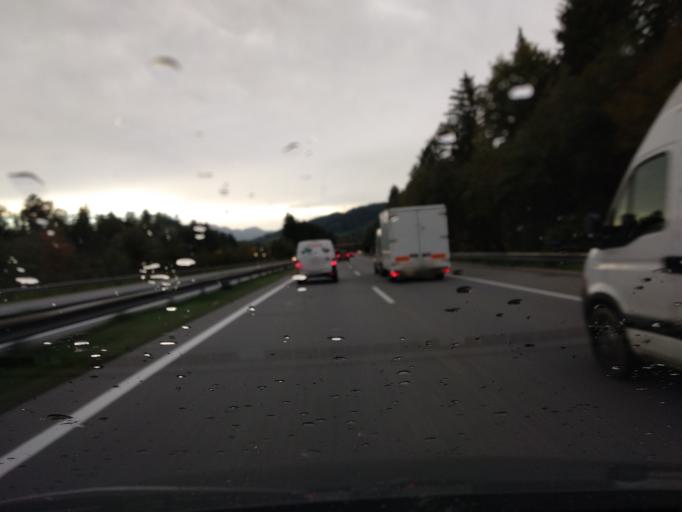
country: AT
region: Vorarlberg
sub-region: Politischer Bezirk Feldkirch
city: Satteins
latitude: 47.2133
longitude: 9.6615
